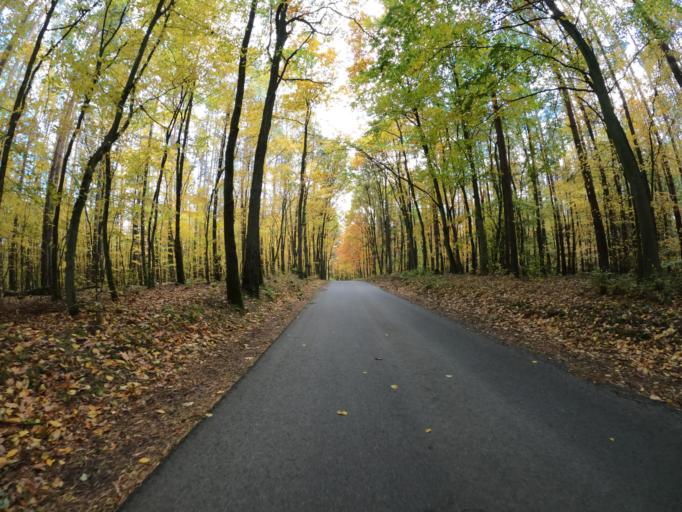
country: PL
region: West Pomeranian Voivodeship
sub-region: Powiat mysliborski
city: Barlinek
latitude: 52.9312
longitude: 15.2865
